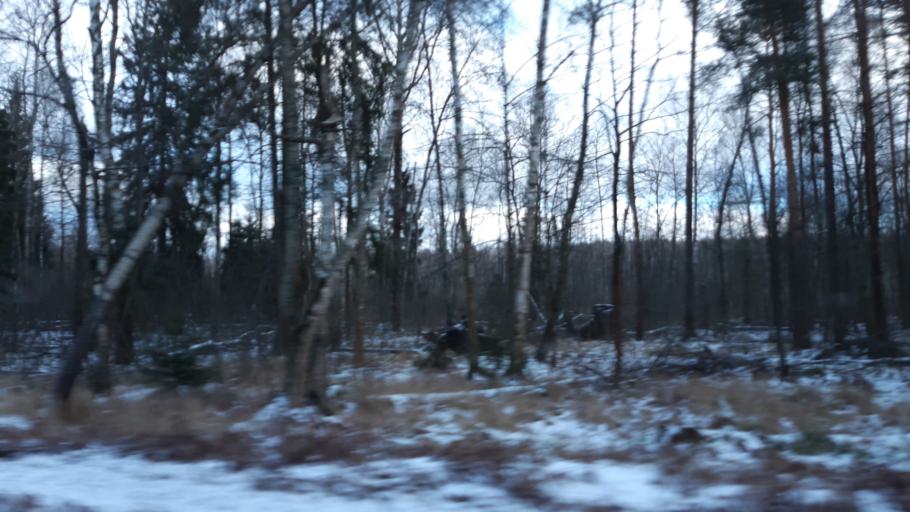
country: RU
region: Moskovskaya
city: Noginsk
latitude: 55.9319
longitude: 38.5437
